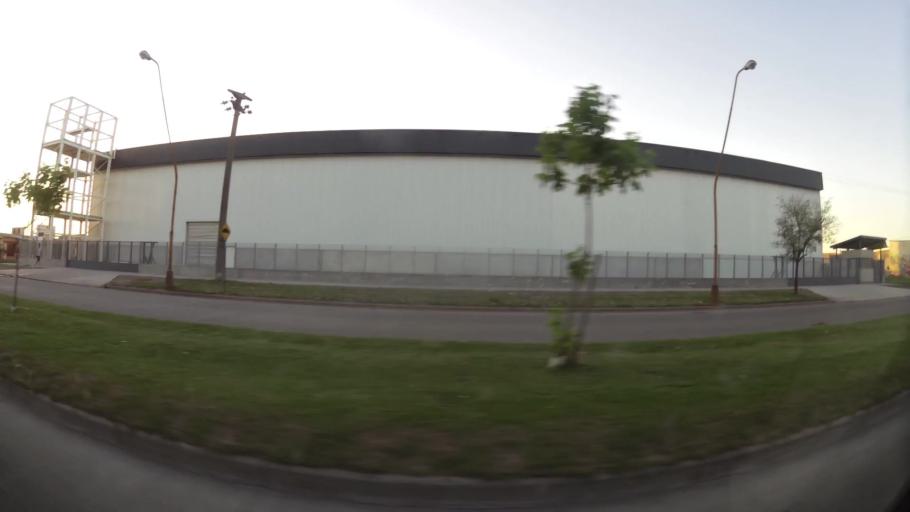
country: AR
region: Santa Fe
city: Santa Fe de la Vera Cruz
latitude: -31.5960
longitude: -60.7002
